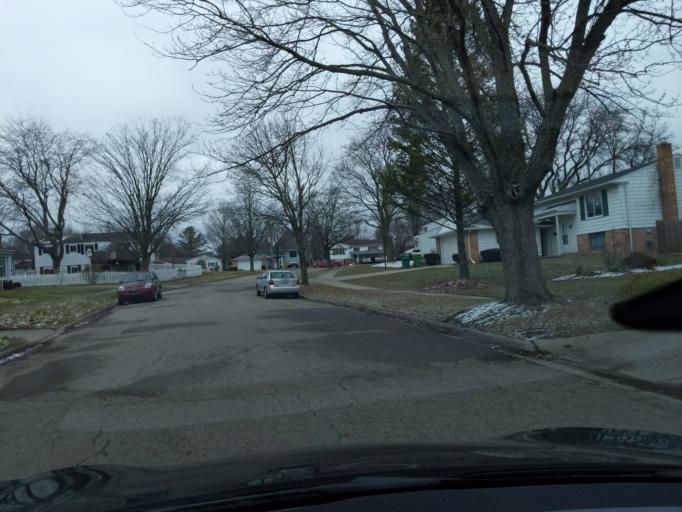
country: US
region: Michigan
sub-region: Ingham County
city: East Lansing
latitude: 42.7532
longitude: -84.5148
